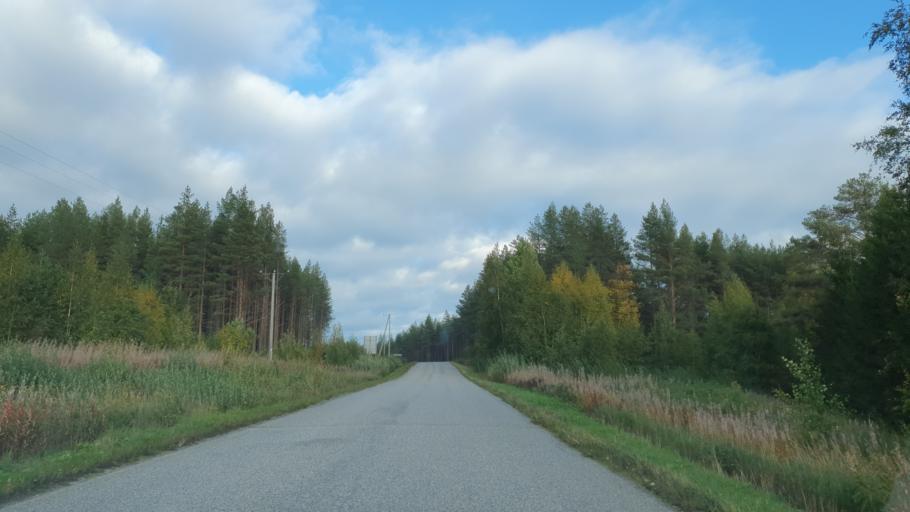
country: FI
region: Kainuu
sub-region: Kehys-Kainuu
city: Kuhmo
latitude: 63.9306
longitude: 29.9767
